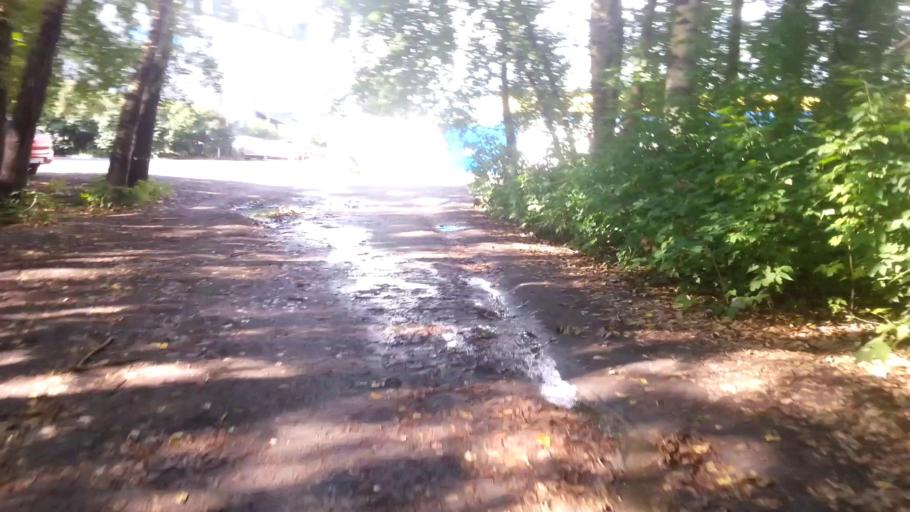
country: RU
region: Altai Krai
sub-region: Gorod Barnaulskiy
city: Barnaul
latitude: 53.3415
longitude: 83.7232
